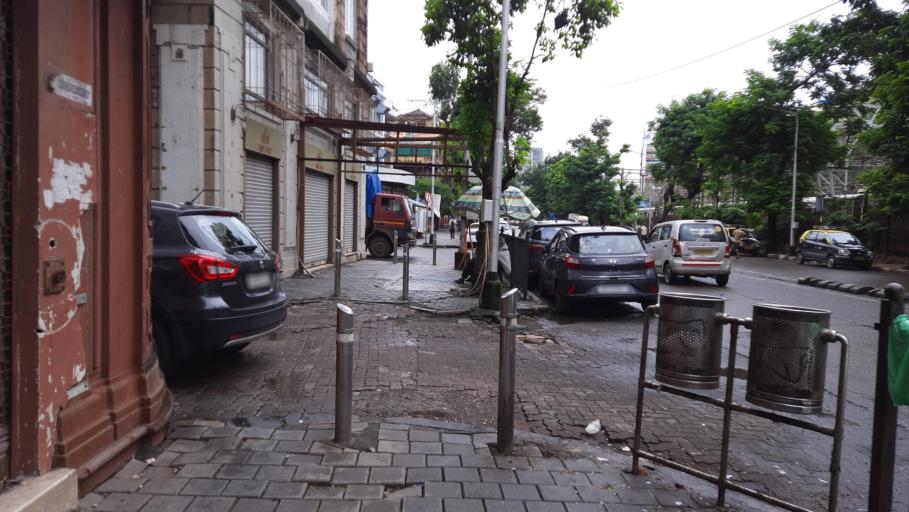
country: IN
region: Maharashtra
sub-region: Raigarh
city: Uran
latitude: 18.9442
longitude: 72.8251
